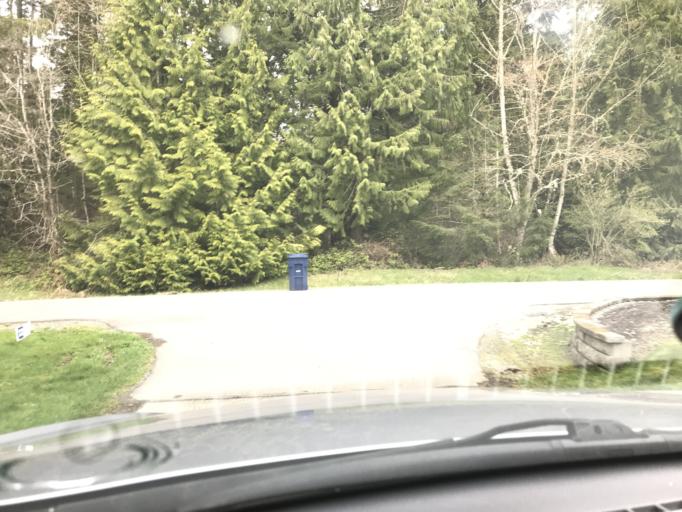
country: US
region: Washington
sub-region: King County
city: Union Hill-Novelty Hill
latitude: 47.6999
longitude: -122.0447
